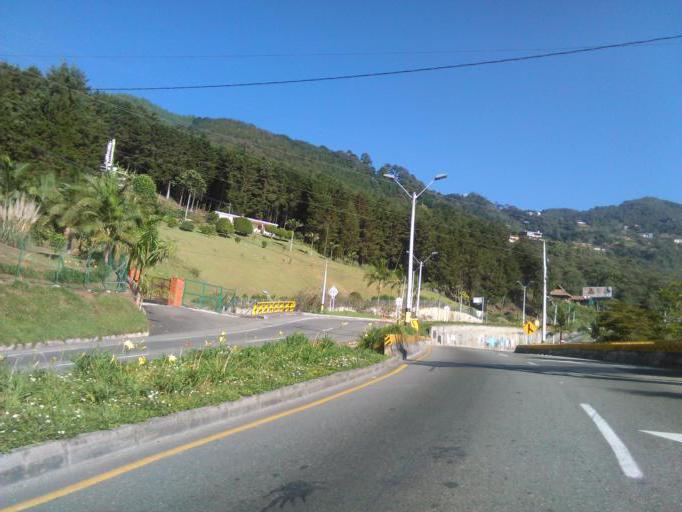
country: CO
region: Antioquia
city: Envigado
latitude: 6.1856
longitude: -75.5464
